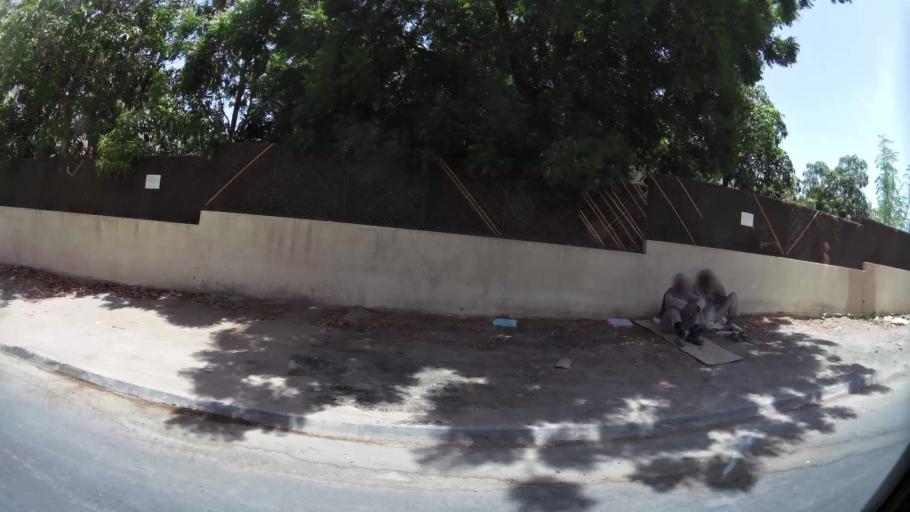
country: OM
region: Muhafazat Masqat
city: Bawshar
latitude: 23.6028
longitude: 58.4568
